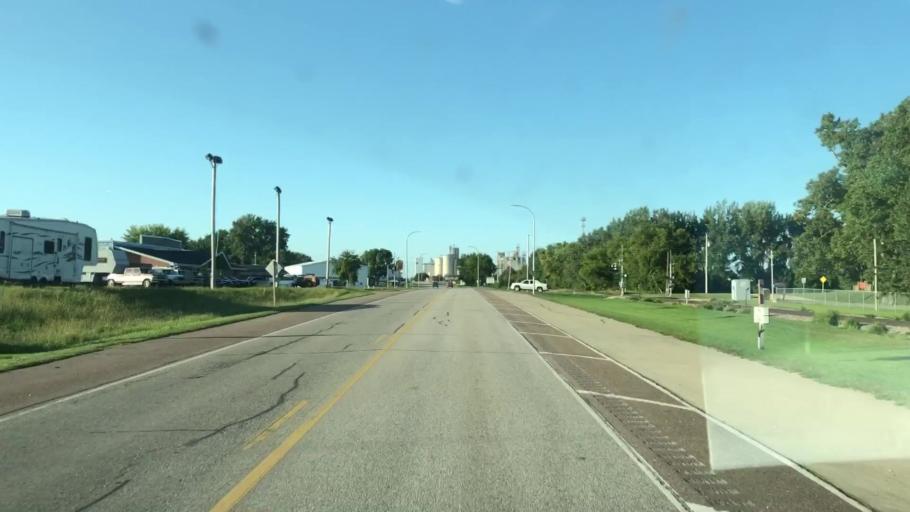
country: US
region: Iowa
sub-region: O'Brien County
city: Sheldon
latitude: 43.1920
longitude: -95.8515
